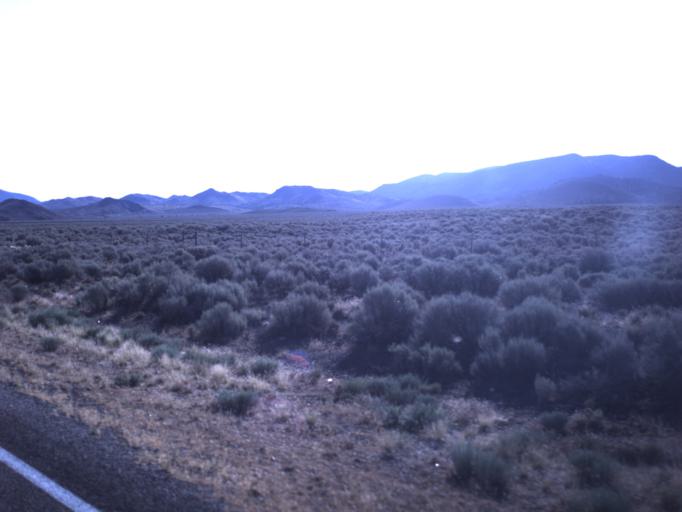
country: US
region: Utah
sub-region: Beaver County
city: Milford
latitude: 38.1792
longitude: -112.9466
